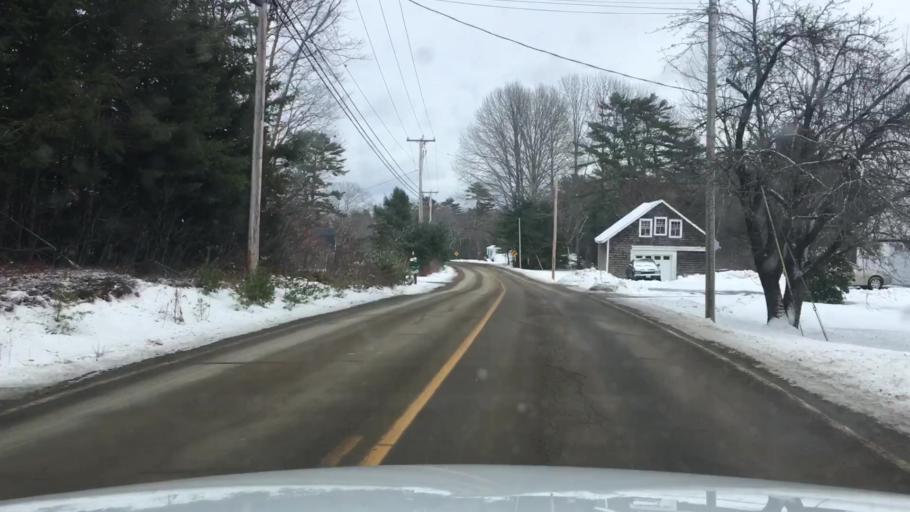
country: US
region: Maine
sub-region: Waldo County
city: Lincolnville
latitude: 44.2866
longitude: -69.0328
